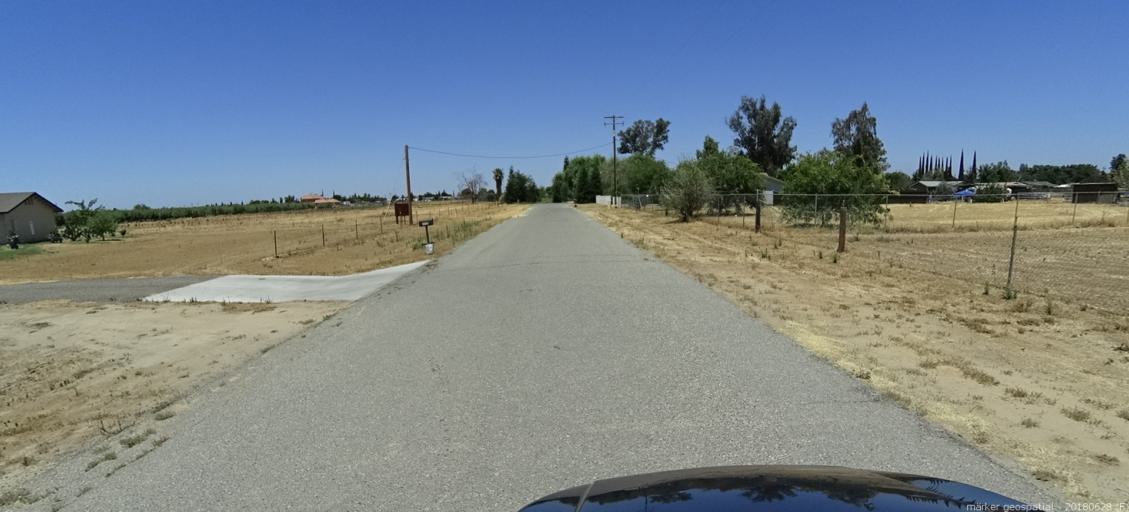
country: US
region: California
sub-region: Madera County
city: Parksdale
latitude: 36.9392
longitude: -120.0319
